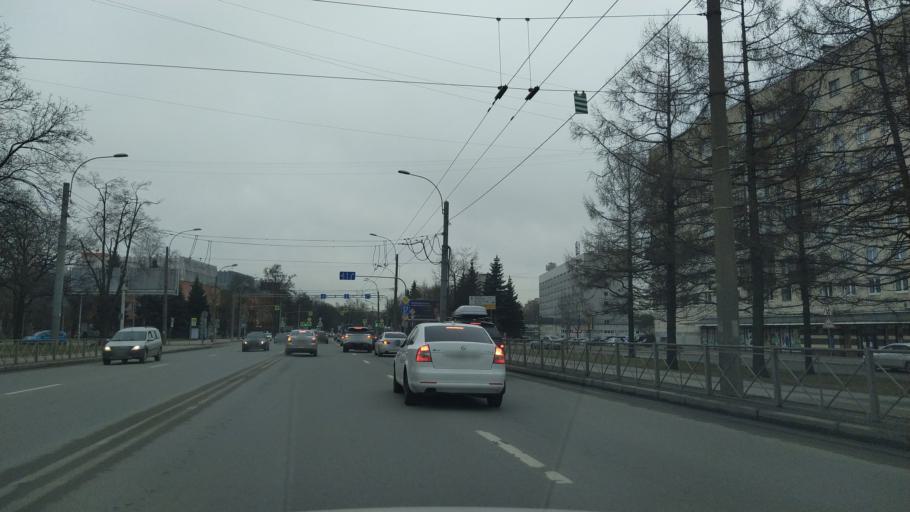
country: RU
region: St.-Petersburg
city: Sosnovka
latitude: 60.0075
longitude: 30.3527
